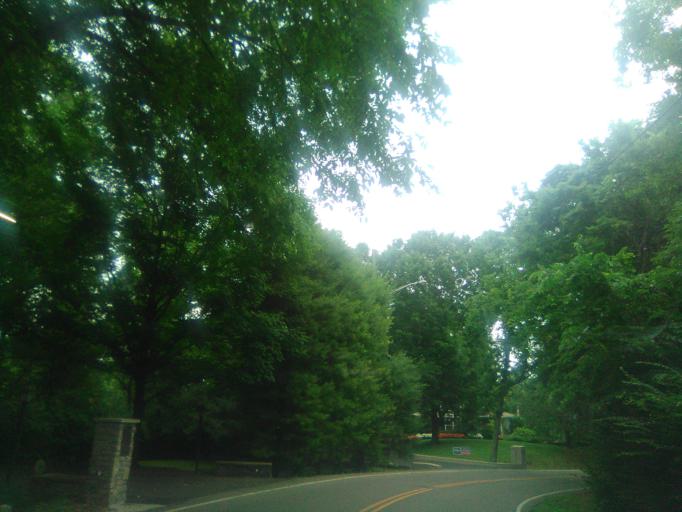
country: US
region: Tennessee
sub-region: Davidson County
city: Belle Meade
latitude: 36.0857
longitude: -86.8949
